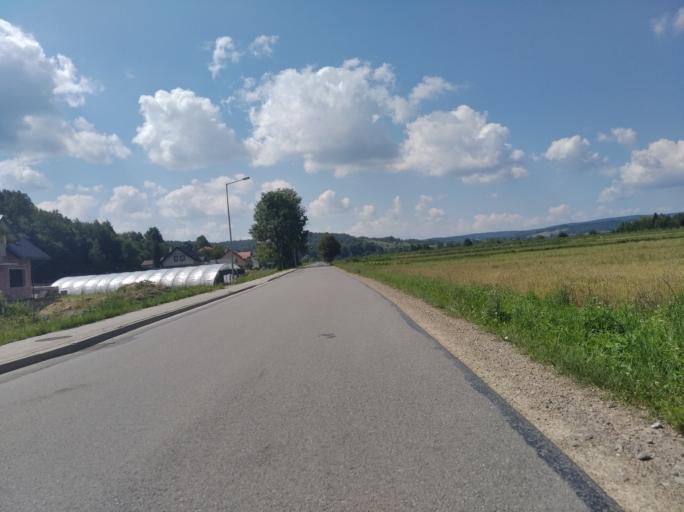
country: PL
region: Subcarpathian Voivodeship
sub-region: Powiat rzeszowski
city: Dynow
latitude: 49.7924
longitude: 22.2410
